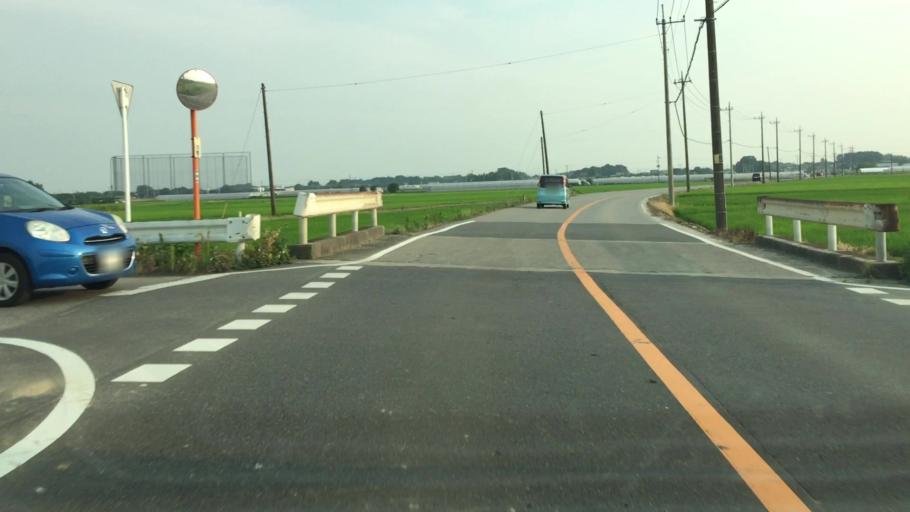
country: JP
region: Tochigi
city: Fujioka
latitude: 36.2440
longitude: 139.5972
